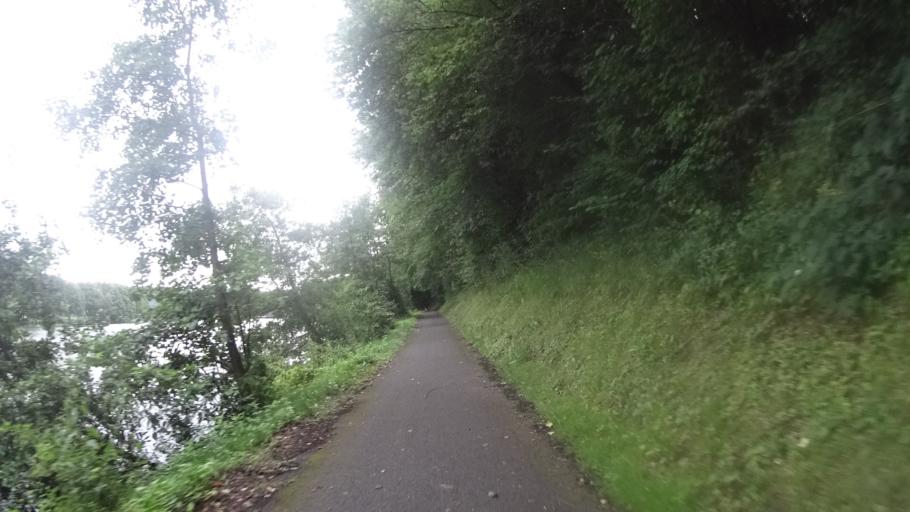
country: FR
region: Lorraine
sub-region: Departement de Meurthe-et-Moselle
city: Gondreville
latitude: 48.6512
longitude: 5.9928
